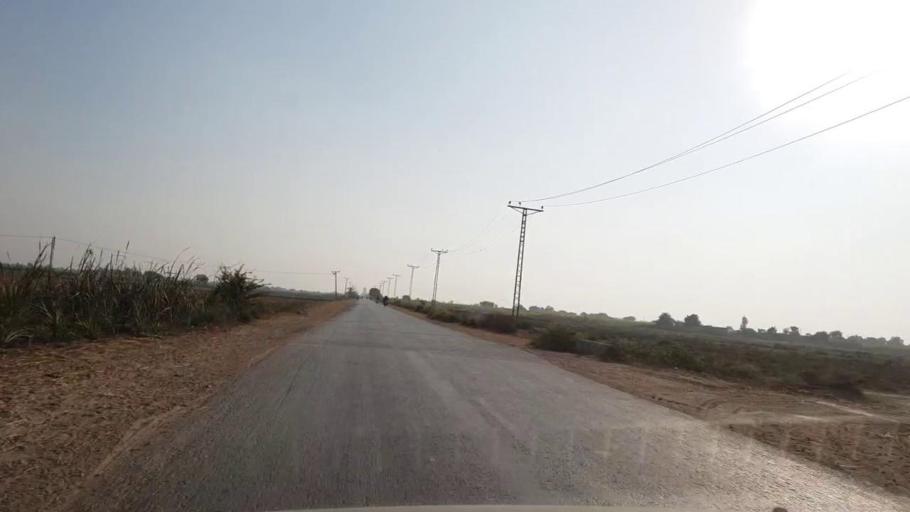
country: PK
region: Sindh
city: Bulri
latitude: 24.8518
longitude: 68.3275
